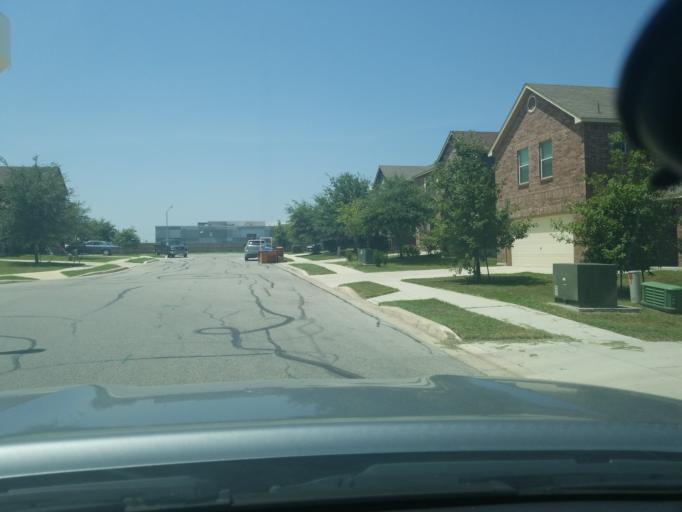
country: US
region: Texas
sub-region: Guadalupe County
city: Northcliff
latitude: 29.5953
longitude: -98.2192
